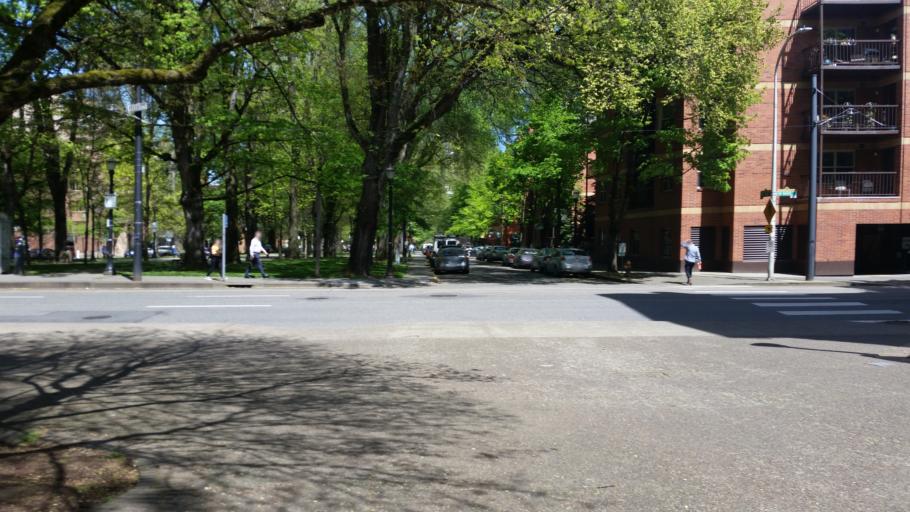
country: US
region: Oregon
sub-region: Multnomah County
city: Portland
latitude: 45.5134
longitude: -122.6840
